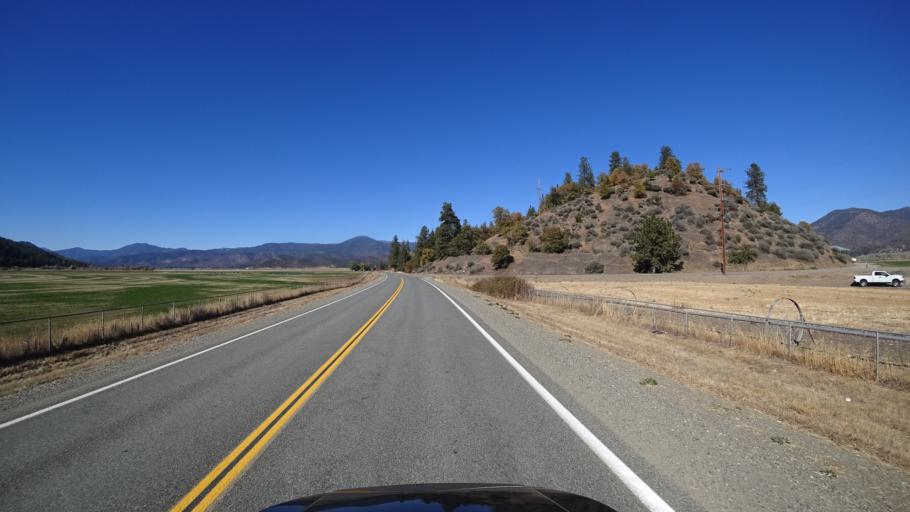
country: US
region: California
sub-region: Siskiyou County
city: Yreka
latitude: 41.6074
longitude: -122.8525
